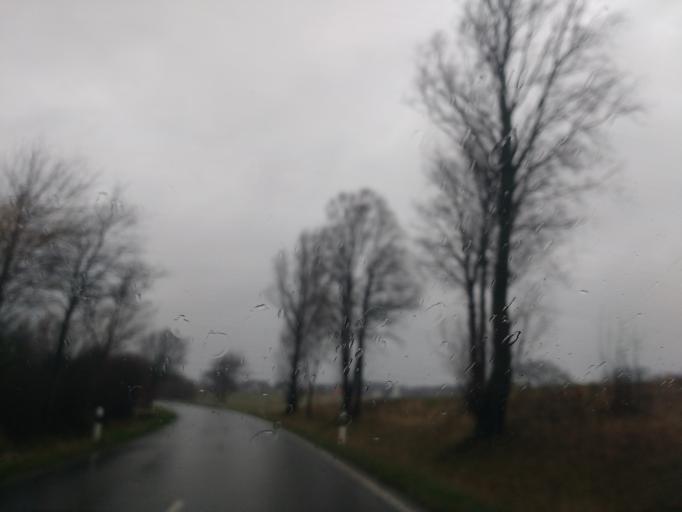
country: DE
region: Schleswig-Holstein
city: Blekendorf
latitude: 54.3132
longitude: 10.6572
